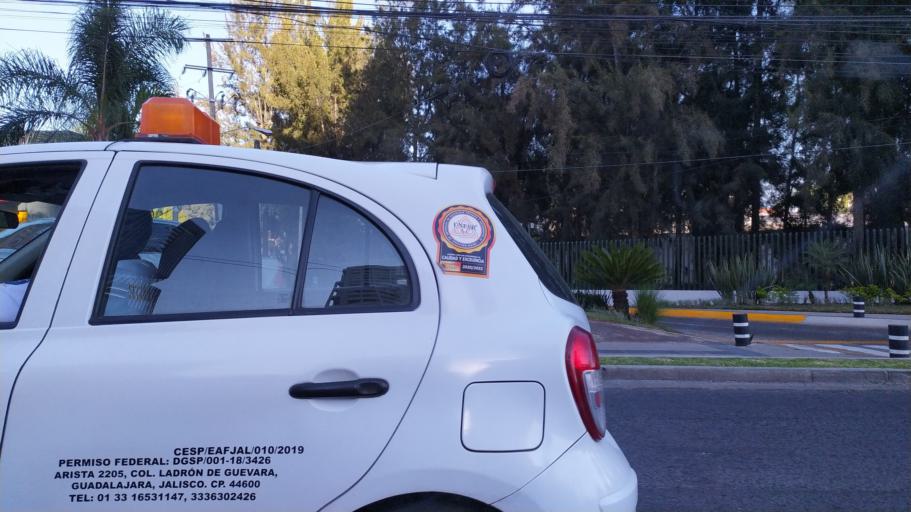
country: MX
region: Jalisco
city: Zapopan2
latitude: 20.7064
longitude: -103.4128
